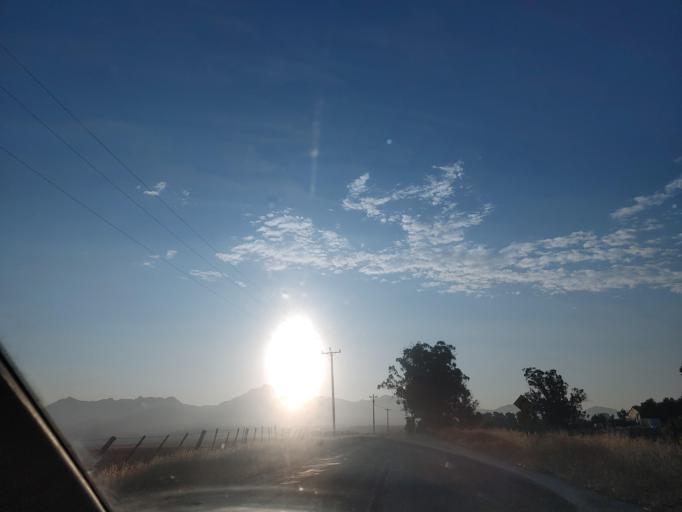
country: US
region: California
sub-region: San Benito County
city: Ridgemark
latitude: 36.8610
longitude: -121.3437
